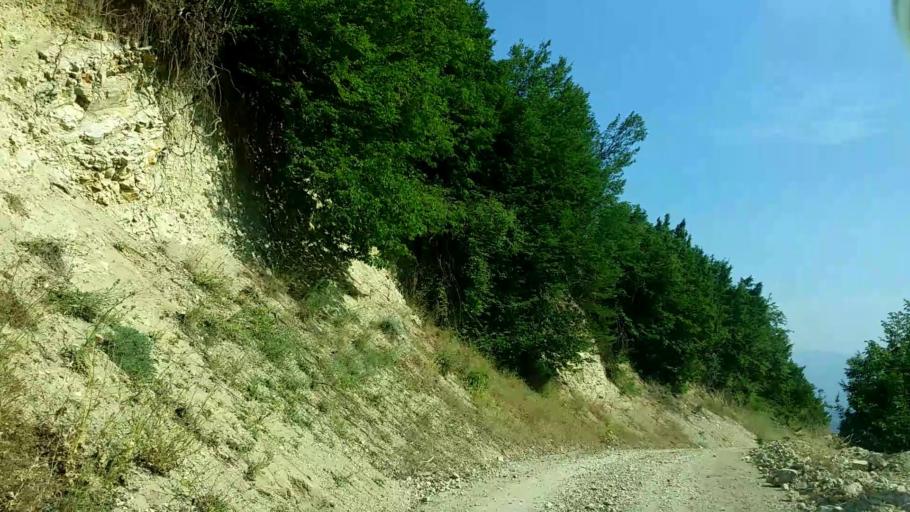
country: IR
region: Mazandaran
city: Chalus
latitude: 36.5533
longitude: 51.2951
